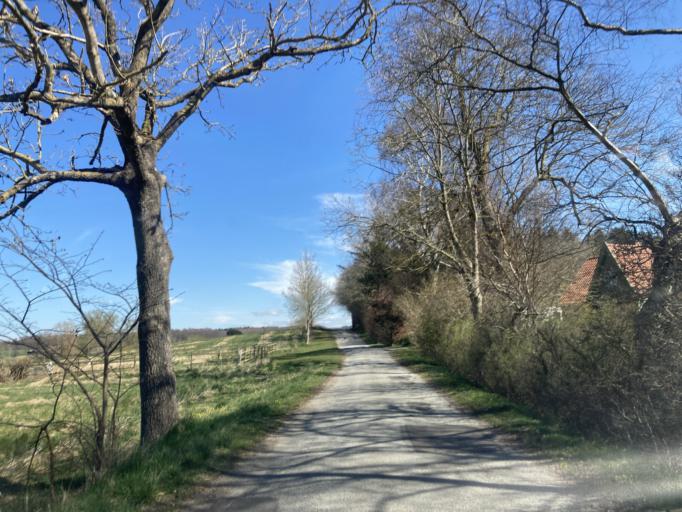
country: DK
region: Capital Region
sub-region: Gribskov Kommune
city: Helsinge
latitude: 55.9994
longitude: 12.2460
